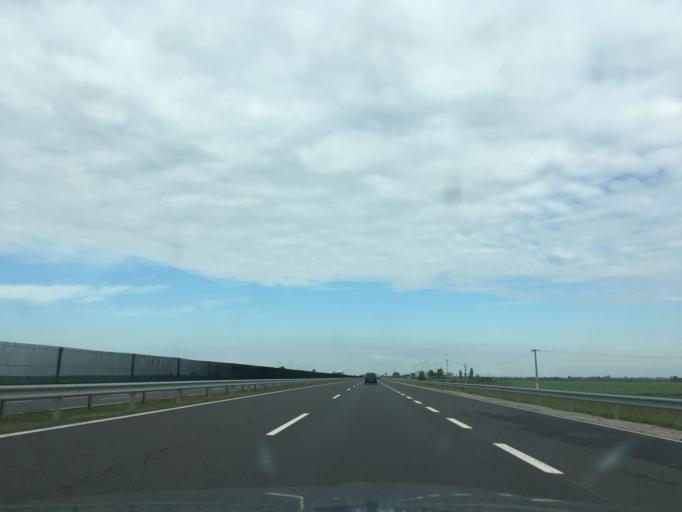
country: HU
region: Hajdu-Bihar
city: Gorbehaza
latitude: 47.7558
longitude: 21.3230
